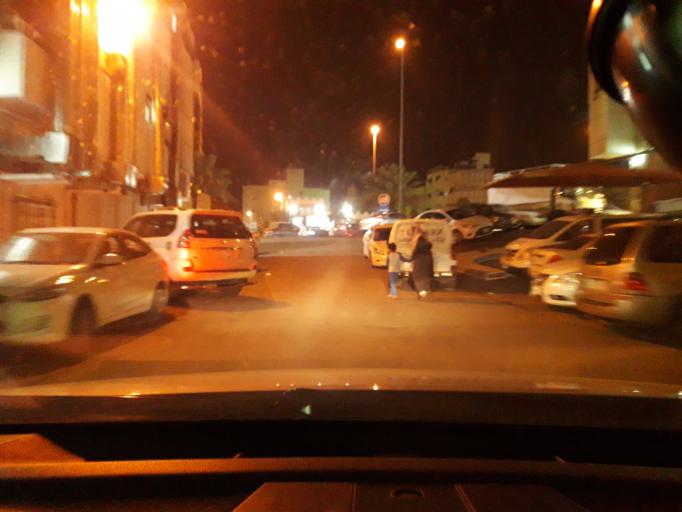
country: SA
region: Al Madinah al Munawwarah
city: Medina
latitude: 24.4687
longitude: 39.6283
